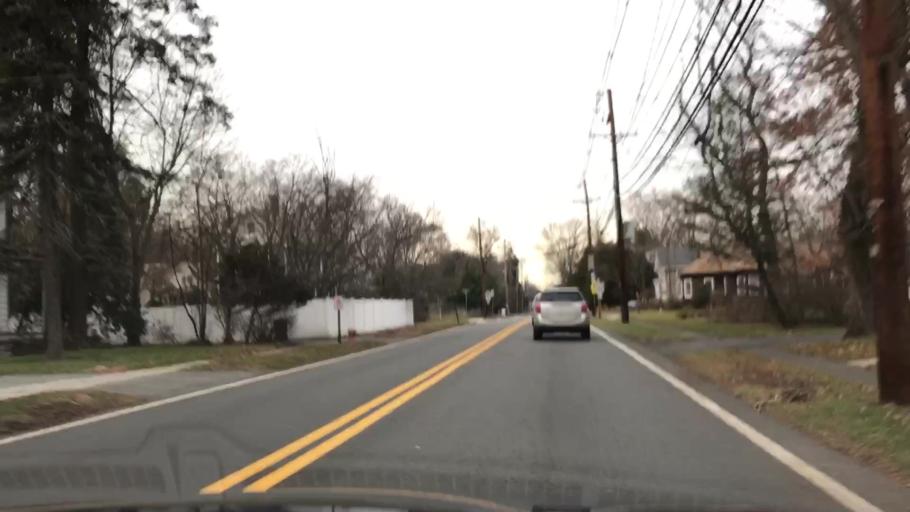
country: US
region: New Jersey
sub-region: Bergen County
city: Norwood
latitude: 40.9925
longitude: -73.9572
